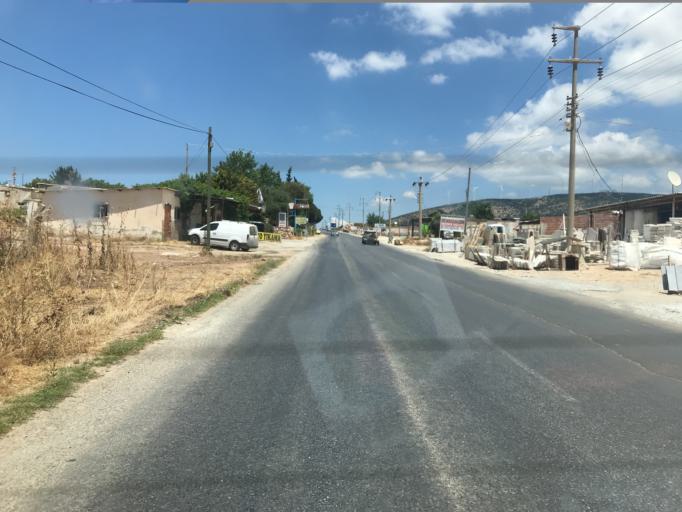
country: TR
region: Aydin
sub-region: Didim
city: Didim
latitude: 37.4186
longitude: 27.3715
